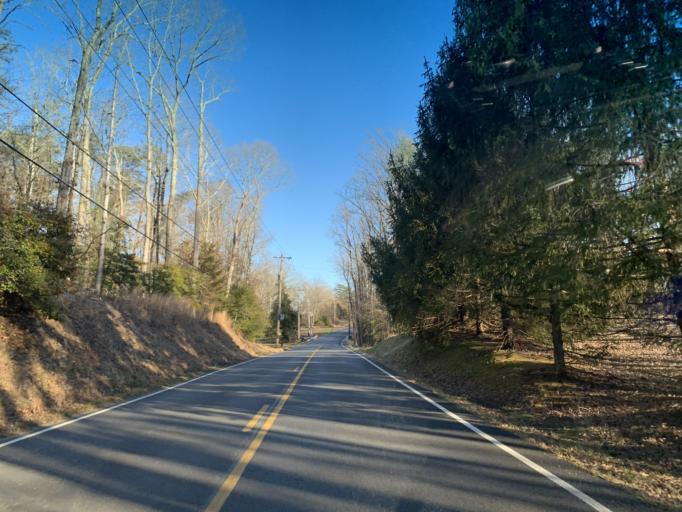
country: US
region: Maryland
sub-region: Saint Mary's County
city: Golden Beach
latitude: 38.4596
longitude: -76.6891
